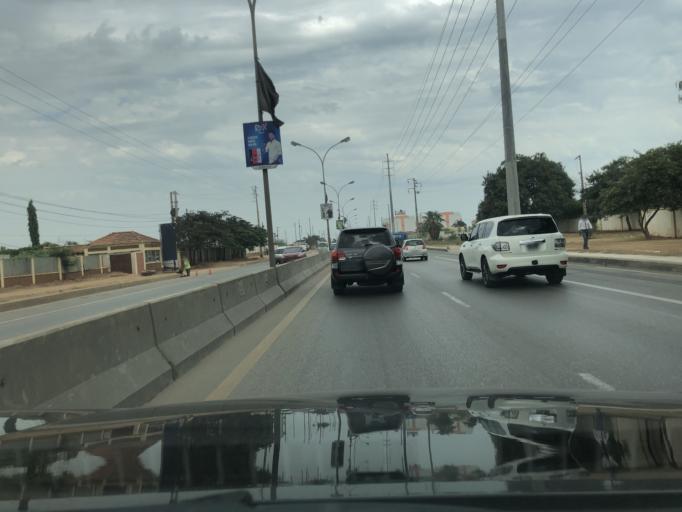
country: AO
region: Luanda
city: Luanda
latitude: -8.9007
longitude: 13.2060
